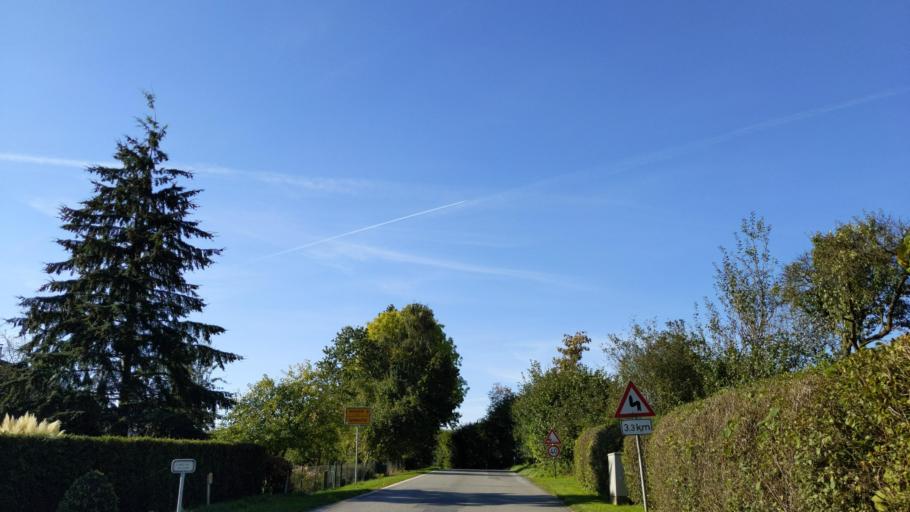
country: DE
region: Schleswig-Holstein
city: Ahrensbok
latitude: 53.9980
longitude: 10.6254
